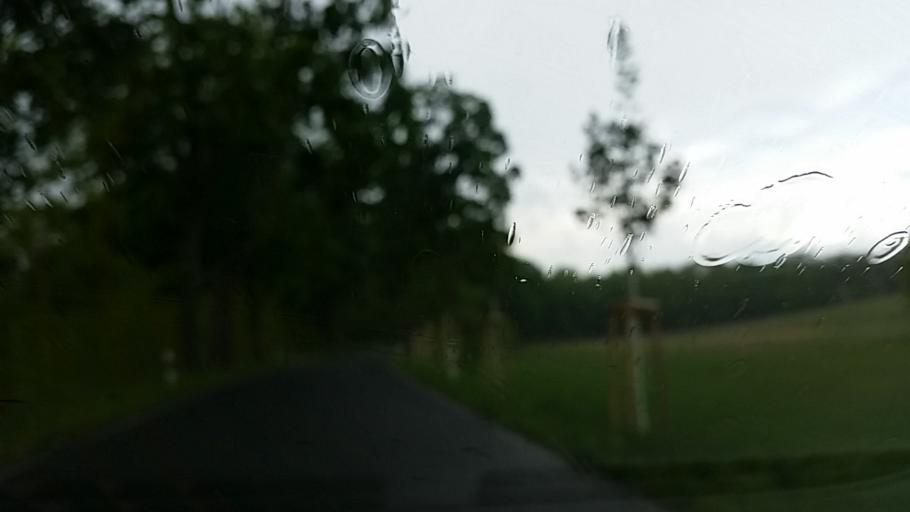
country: DE
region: Brandenburg
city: Diensdorf-Radlow
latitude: 52.2508
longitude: 14.0369
